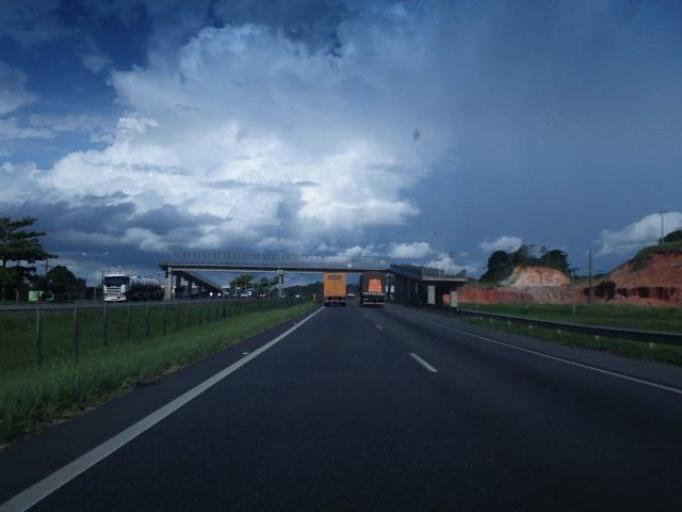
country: BR
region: Sao Paulo
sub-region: Juquia
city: Juquia
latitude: -24.3317
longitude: -47.6330
